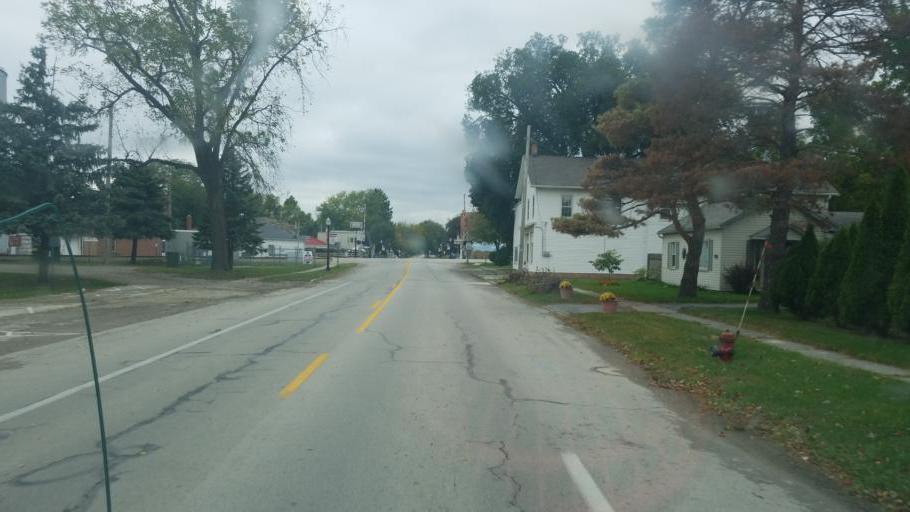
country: US
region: Ohio
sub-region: Wood County
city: Haskins
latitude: 41.4634
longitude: -83.7045
